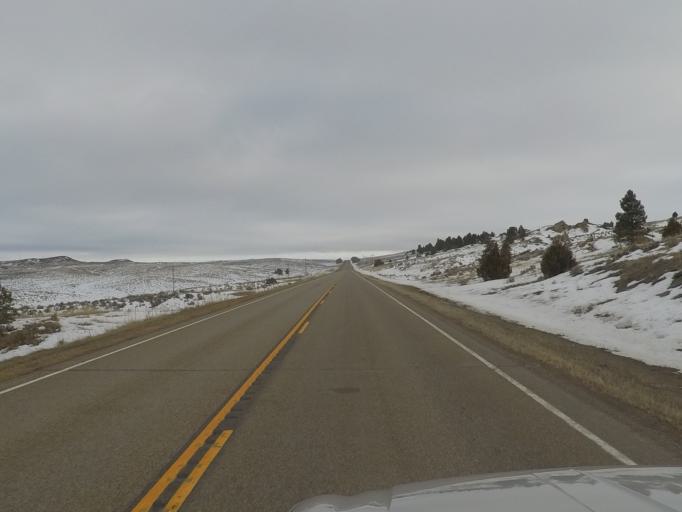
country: US
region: Montana
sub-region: Golden Valley County
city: Ryegate
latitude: 46.2582
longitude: -108.9371
